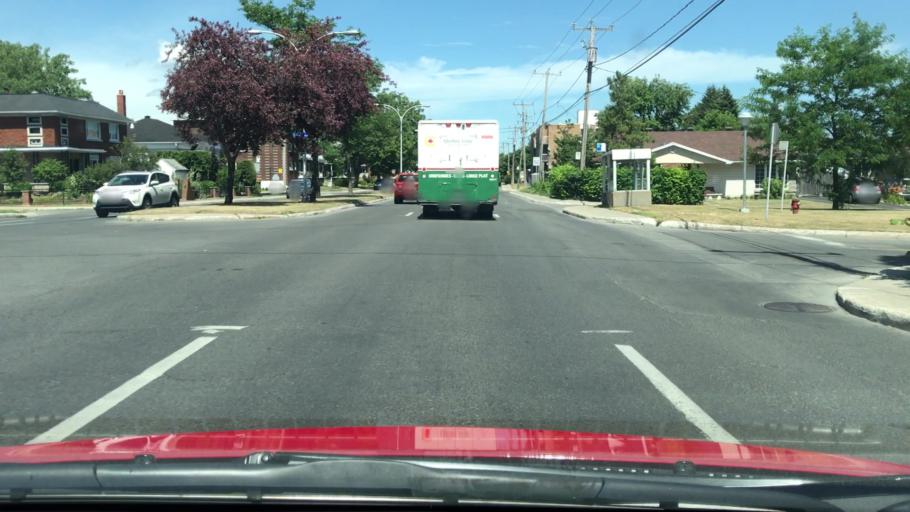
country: CA
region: Quebec
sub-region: Laval
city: Laval
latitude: 45.5341
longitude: -73.7493
